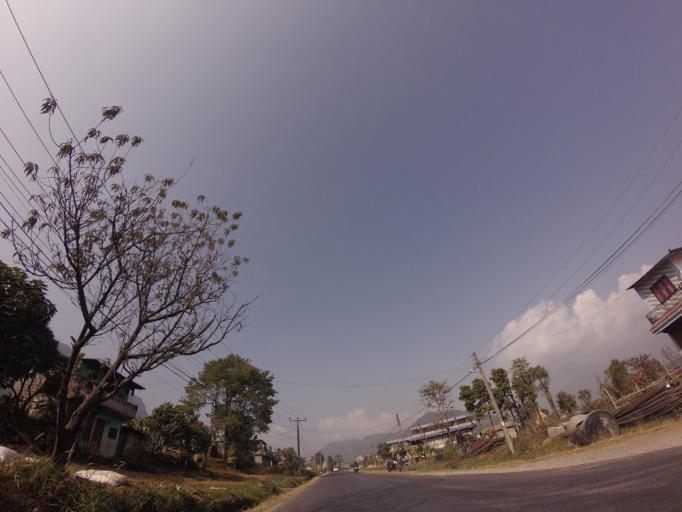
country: NP
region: Western Region
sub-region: Gandaki Zone
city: Pokhara
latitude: 28.2735
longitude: 83.9423
